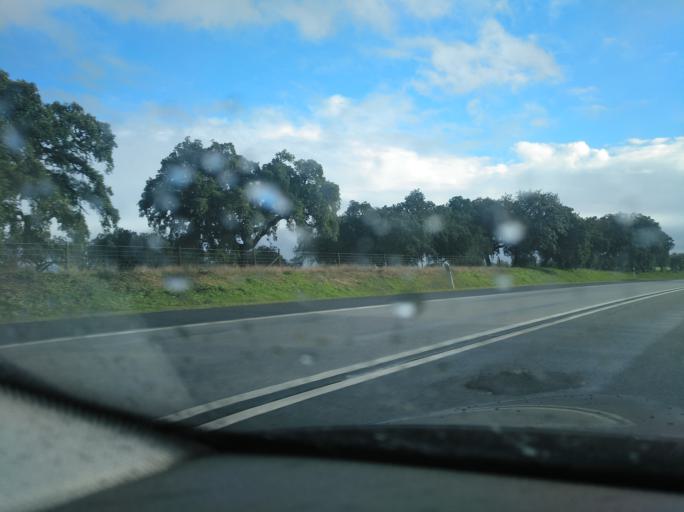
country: PT
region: Setubal
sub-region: Grandola
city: Grandola
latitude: 38.0530
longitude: -8.4027
